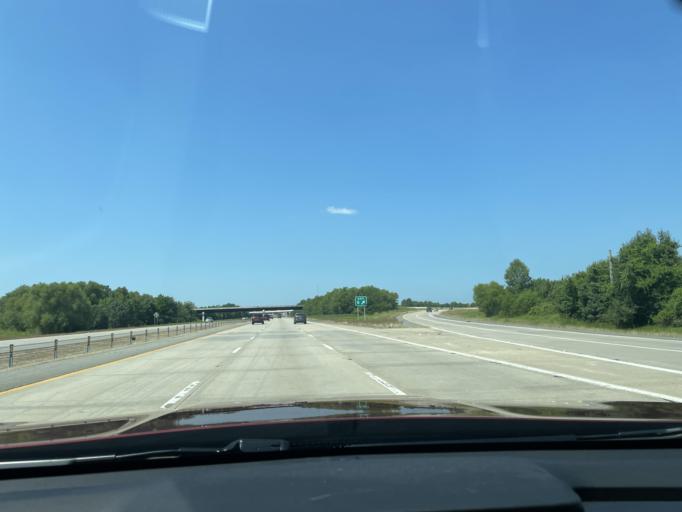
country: US
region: Arkansas
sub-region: Pulaski County
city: Jacksonville
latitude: 34.8465
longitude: -92.1501
